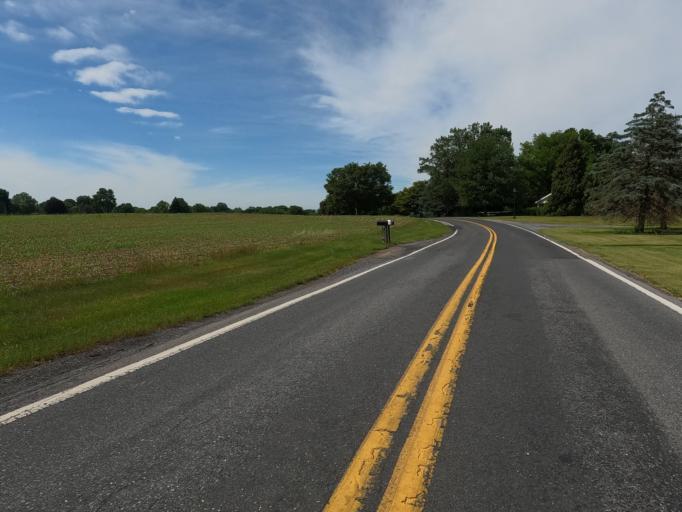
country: US
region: Pennsylvania
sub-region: Dauphin County
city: Palmdale
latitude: 40.2638
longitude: -76.6170
